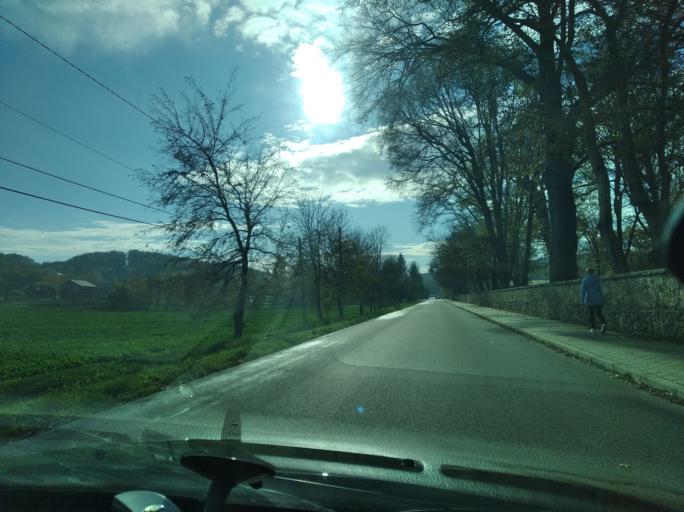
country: PL
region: Subcarpathian Voivodeship
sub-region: Powiat debicki
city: Brzeznica
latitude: 50.0573
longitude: 21.4841
